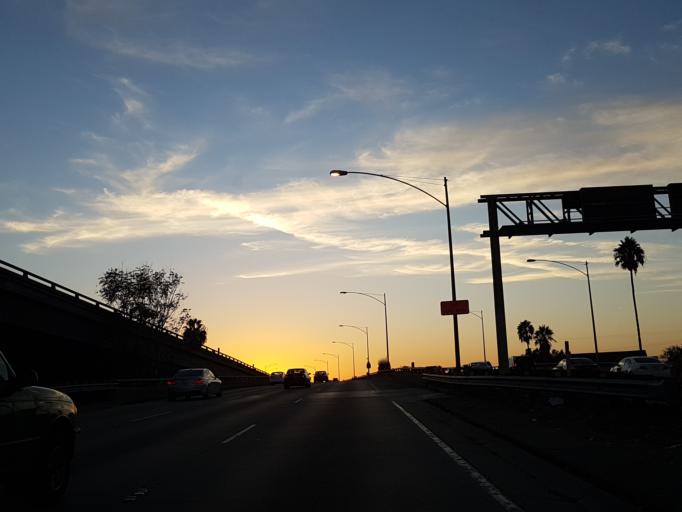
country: US
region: California
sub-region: Los Angeles County
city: Los Angeles
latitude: 34.0384
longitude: -118.2774
